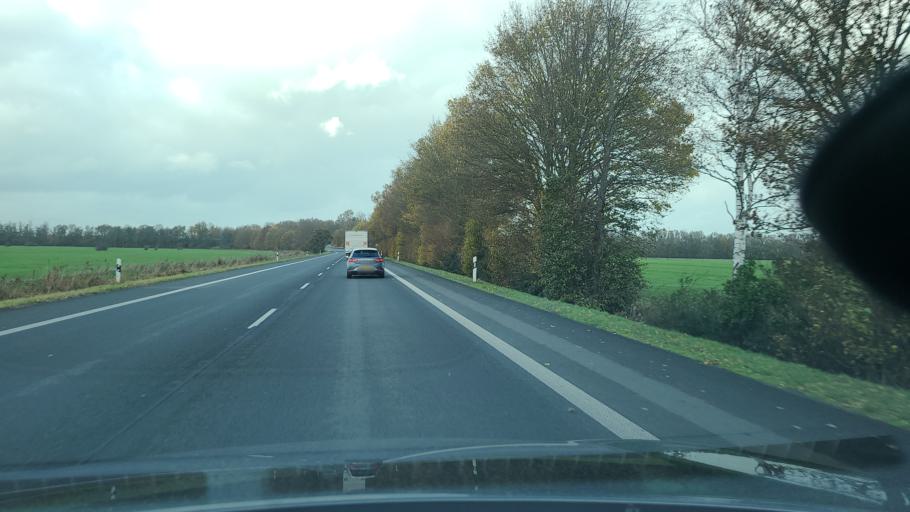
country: DE
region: North Rhine-Westphalia
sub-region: Regierungsbezirk Dusseldorf
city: Kranenburg
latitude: 51.7951
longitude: 6.0245
